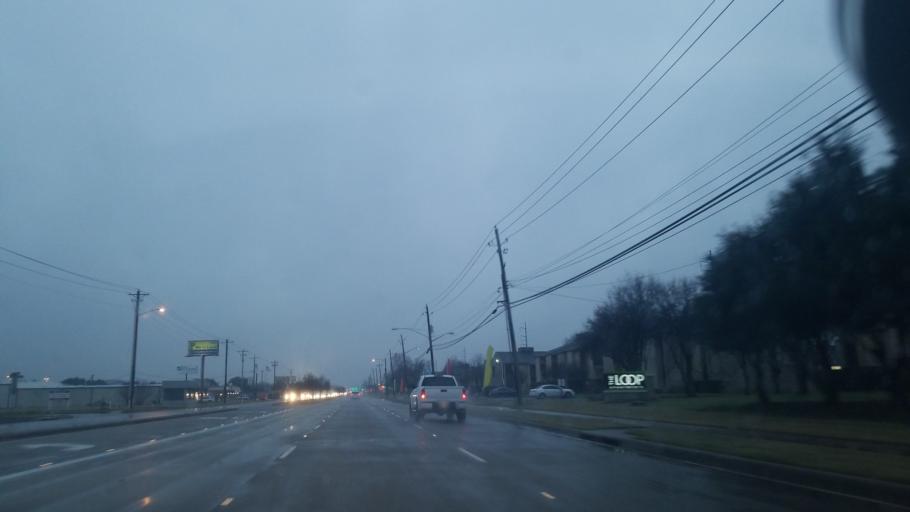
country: US
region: Texas
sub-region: Denton County
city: Denton
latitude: 33.2203
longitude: -97.0905
